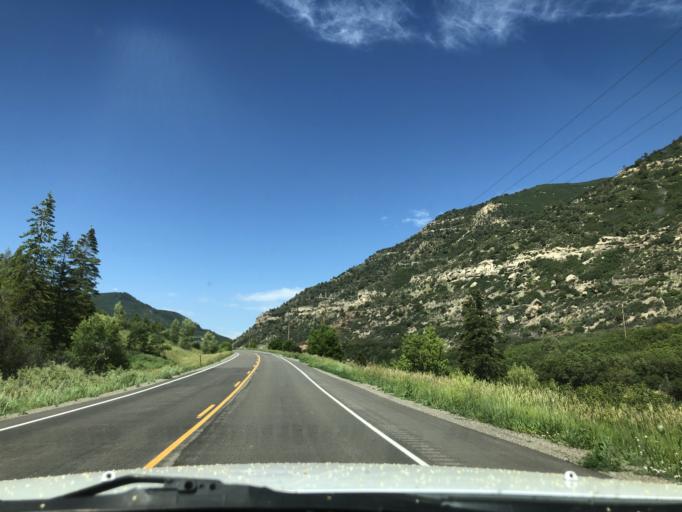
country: US
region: Colorado
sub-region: Delta County
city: Paonia
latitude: 38.9305
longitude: -107.4154
